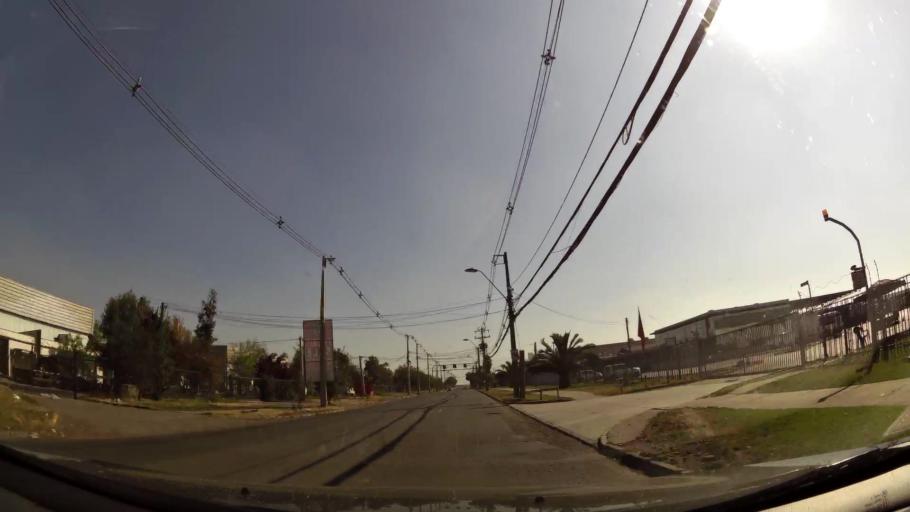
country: CL
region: Santiago Metropolitan
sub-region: Provincia de Chacabuco
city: Chicureo Abajo
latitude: -33.3371
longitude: -70.7242
